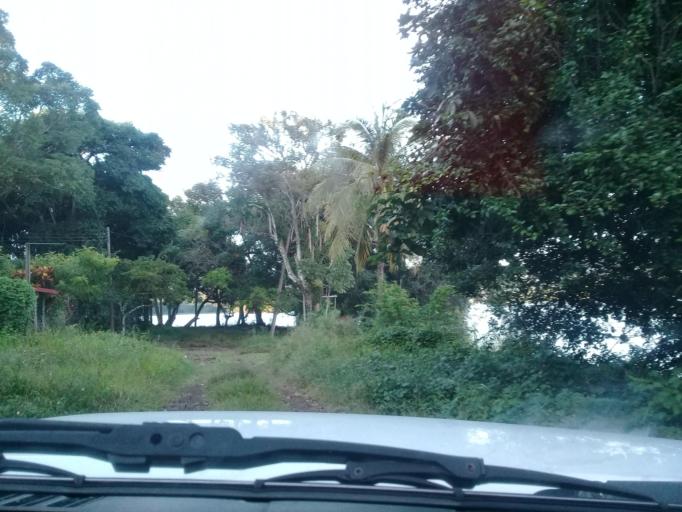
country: MX
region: Veracruz
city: Catemaco
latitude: 18.4363
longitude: -95.0806
